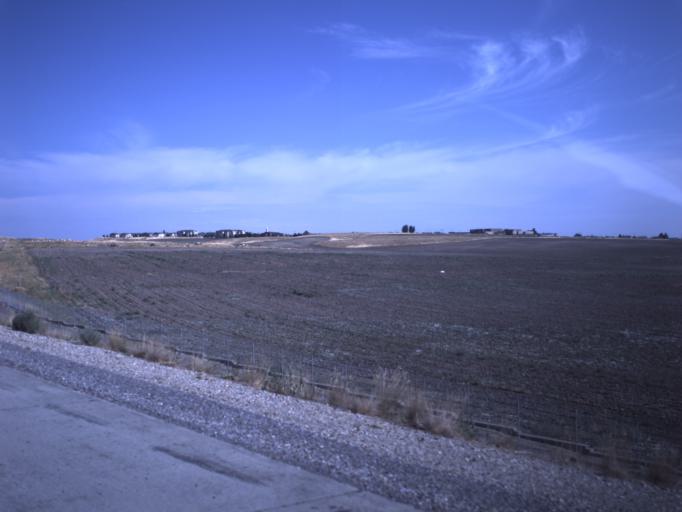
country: US
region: Utah
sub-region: Salt Lake County
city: Oquirrh
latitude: 40.6118
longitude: -112.0356
